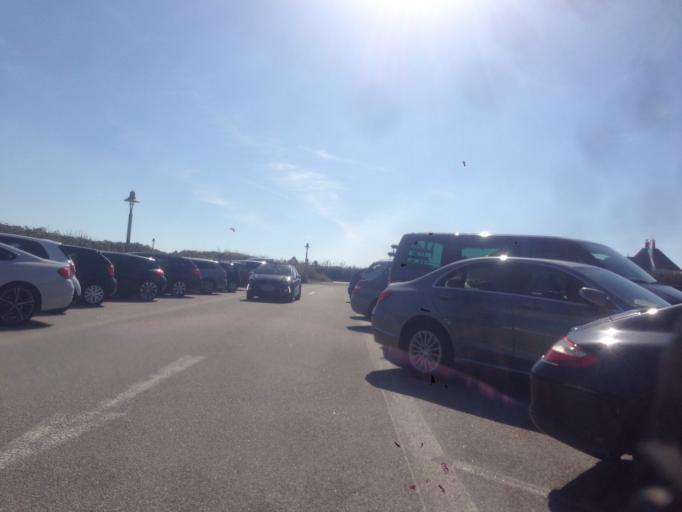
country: DE
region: Schleswig-Holstein
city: Westerland
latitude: 54.9623
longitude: 8.3343
